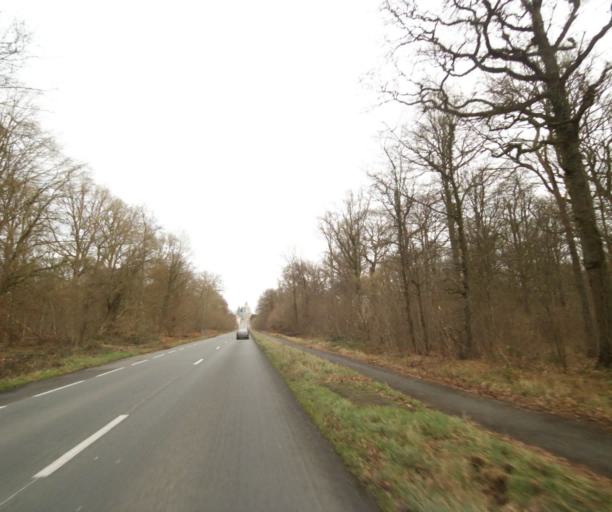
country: BE
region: Wallonia
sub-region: Province du Hainaut
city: Peruwelz
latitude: 50.4902
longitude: 3.6046
